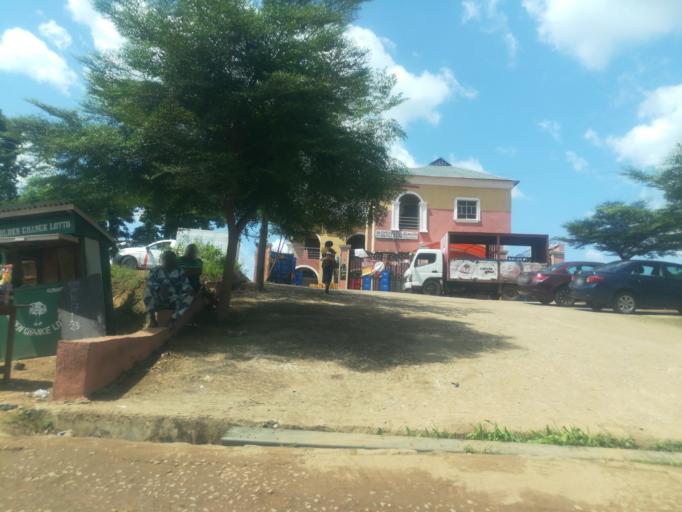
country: NG
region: Oyo
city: Lalupon
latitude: 7.4423
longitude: 4.0106
